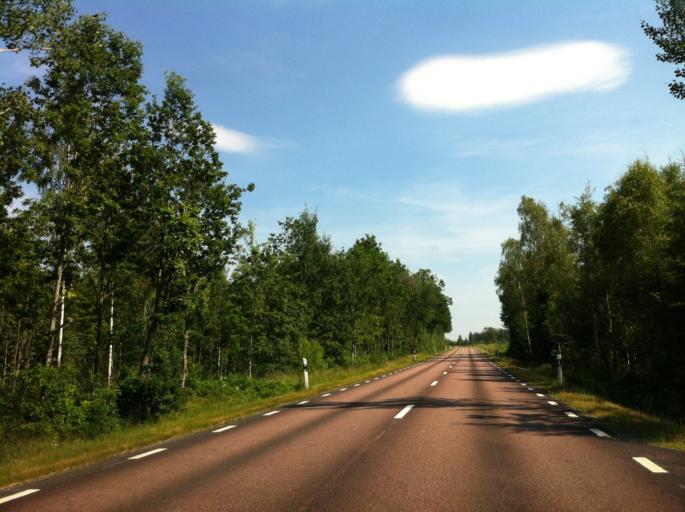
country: SE
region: Kalmar
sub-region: Nybro Kommun
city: Nybro
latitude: 56.7862
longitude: 15.8045
